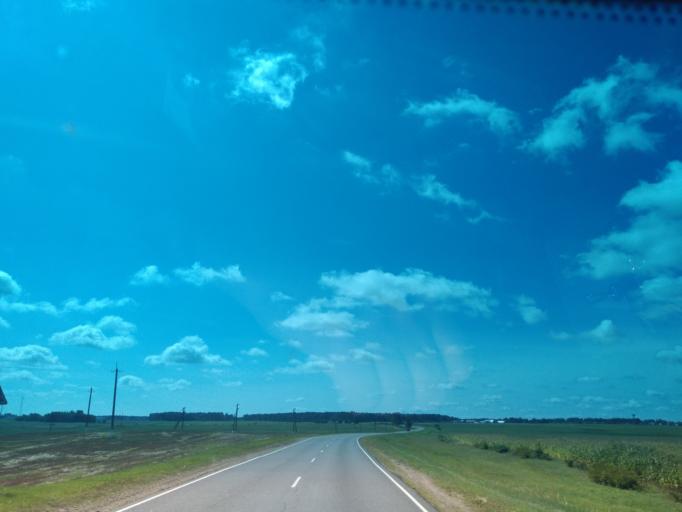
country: BY
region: Minsk
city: Uzda
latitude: 53.3685
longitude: 27.2318
